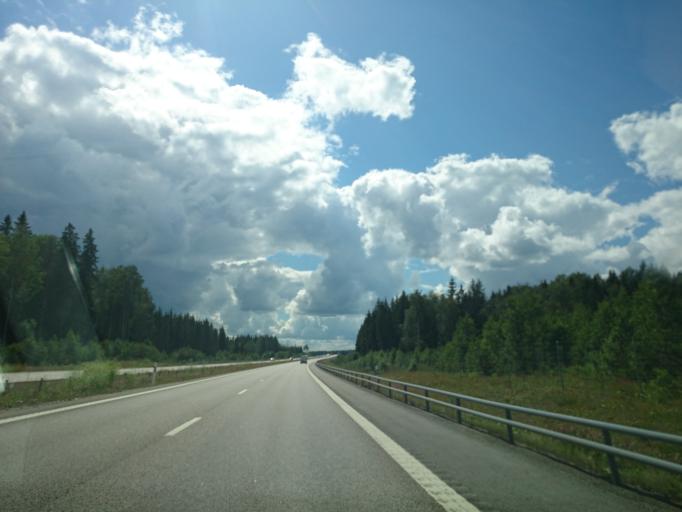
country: SE
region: Uppsala
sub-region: Tierps Kommun
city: Tierp
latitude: 60.3694
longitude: 17.4798
